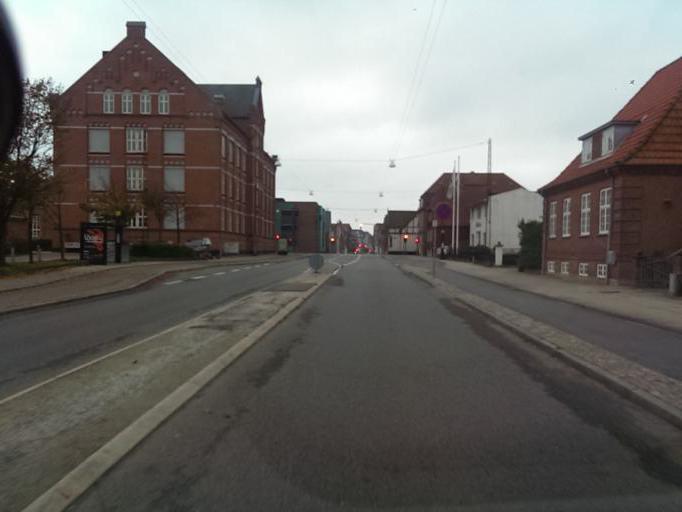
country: DK
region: South Denmark
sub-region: Esbjerg Kommune
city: Esbjerg
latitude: 55.4713
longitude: 8.4450
